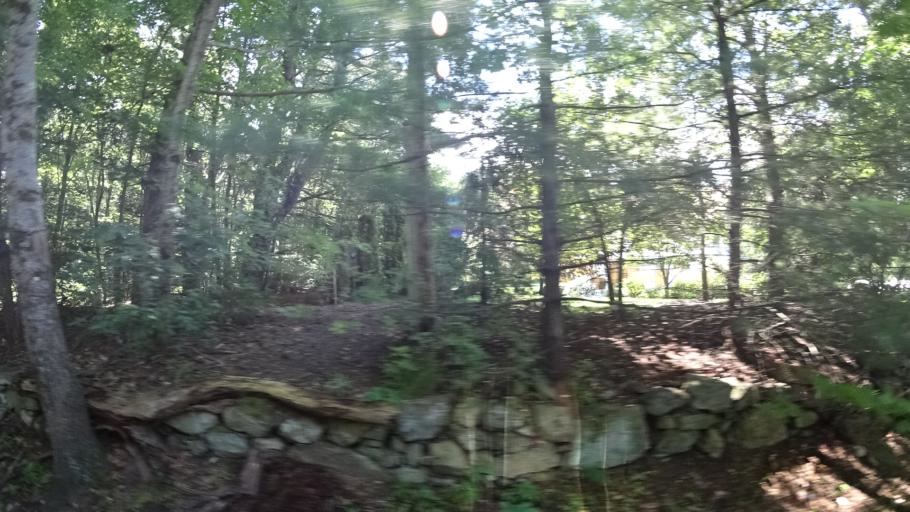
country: US
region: Massachusetts
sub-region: Norfolk County
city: Dedham
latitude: 42.2468
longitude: -71.1863
